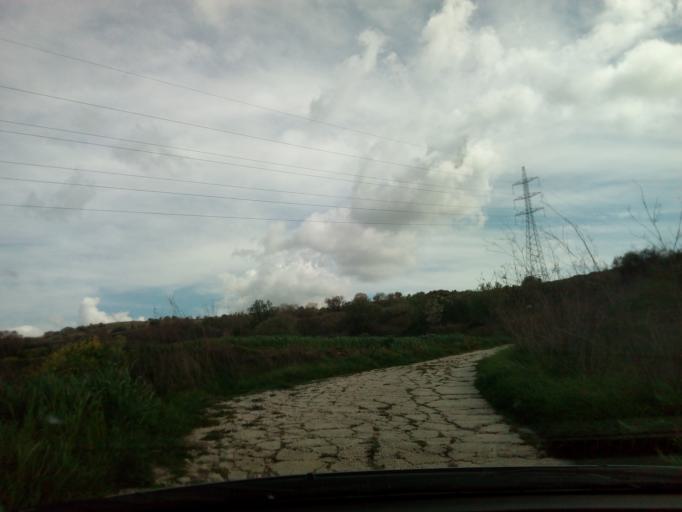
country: CY
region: Pafos
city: Tala
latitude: 34.8985
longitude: 32.4923
